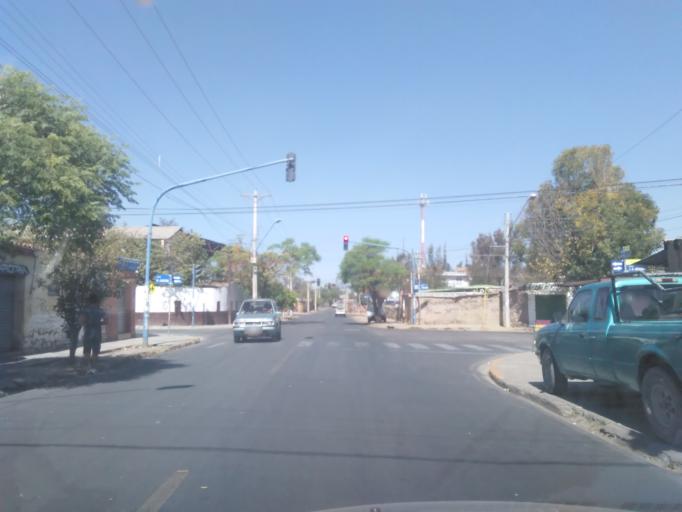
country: BO
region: Cochabamba
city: Cochabamba
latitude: -17.3978
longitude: -66.1400
